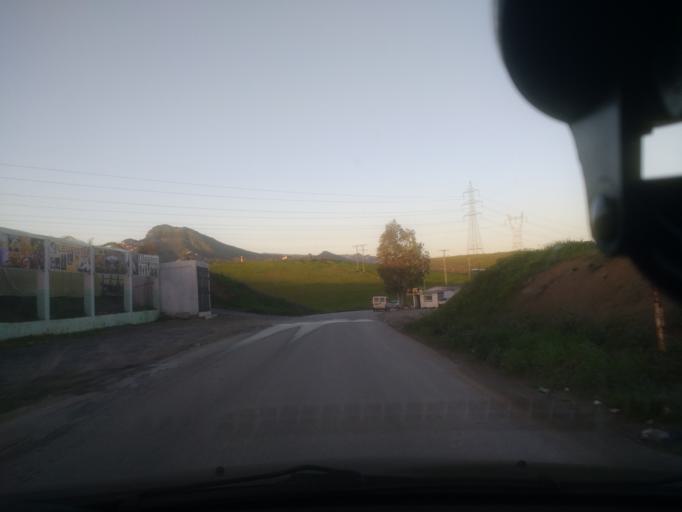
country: DZ
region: Boumerdes
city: Makouda
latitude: 36.7596
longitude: 4.0540
